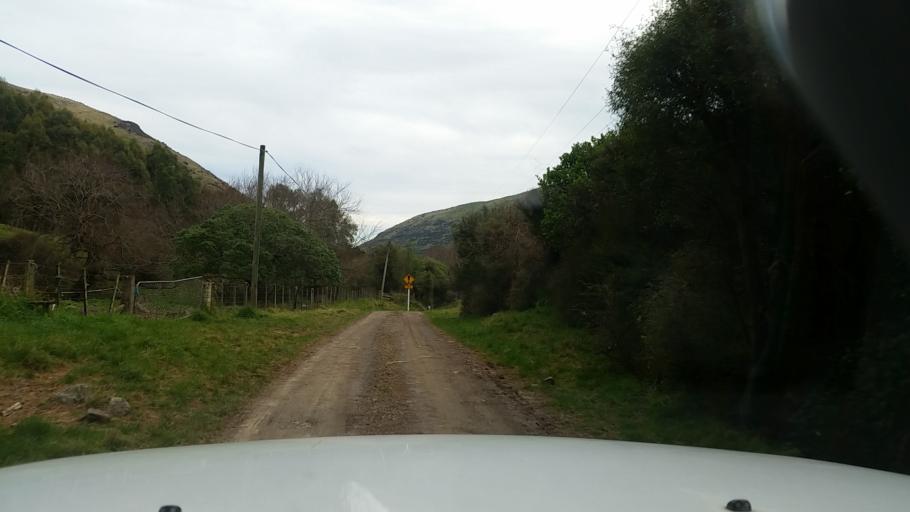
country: NZ
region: Canterbury
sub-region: Christchurch City
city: Christchurch
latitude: -43.7598
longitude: 172.7271
